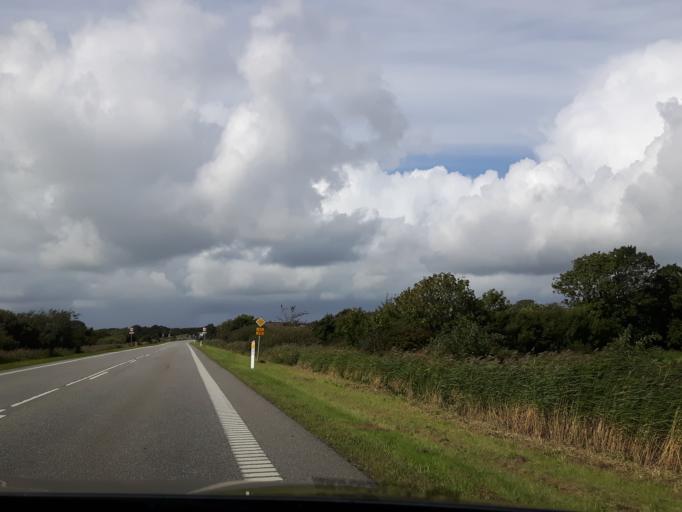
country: DK
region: North Denmark
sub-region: Vesthimmerland Kommune
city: Logstor
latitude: 57.0250
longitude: 9.0121
